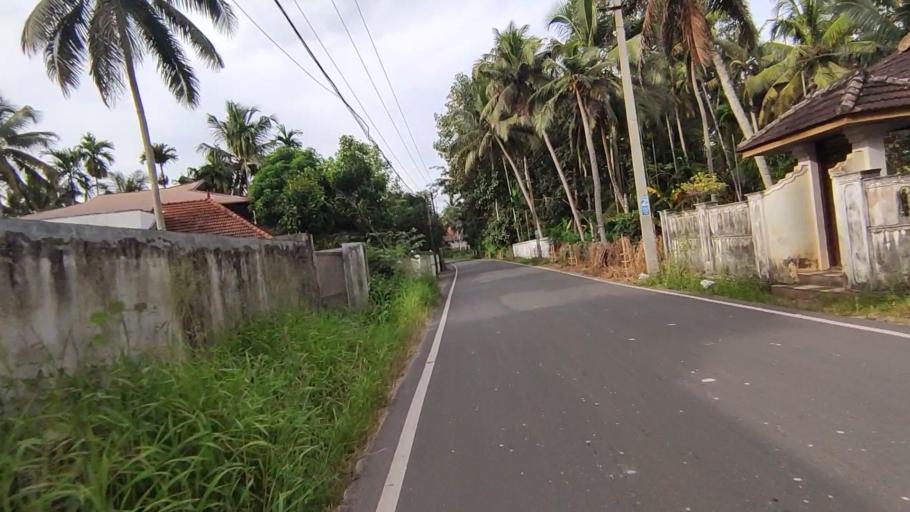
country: IN
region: Kerala
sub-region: Kottayam
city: Kottayam
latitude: 9.6010
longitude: 76.5034
